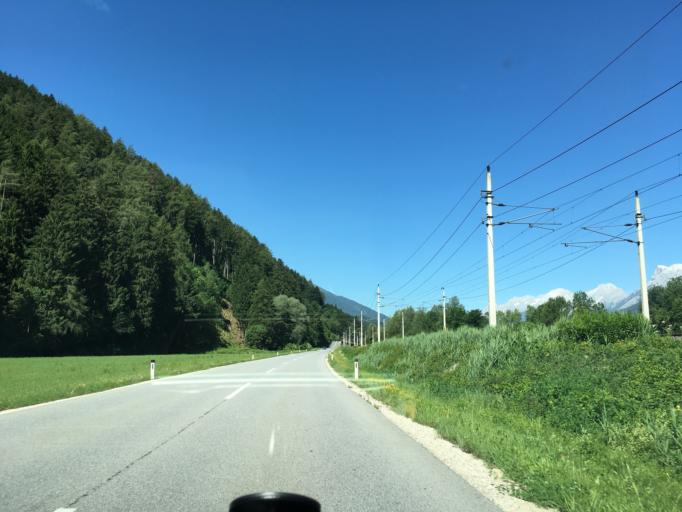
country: AT
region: Tyrol
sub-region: Politischer Bezirk Innsbruck Land
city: Unterperfuss
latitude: 47.2607
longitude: 11.2507
